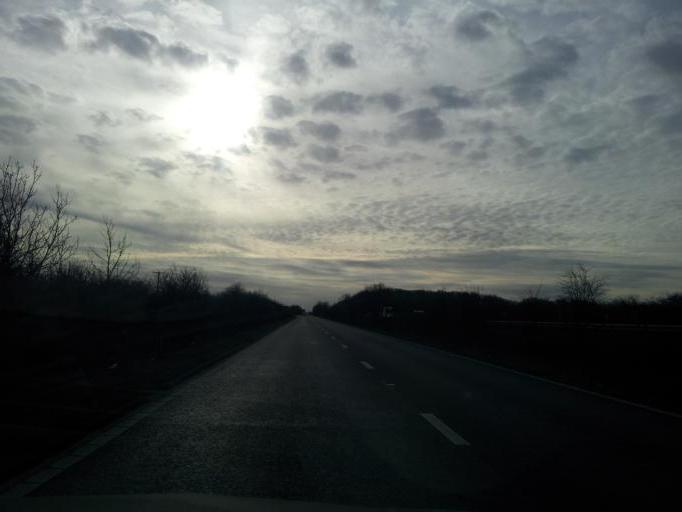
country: GB
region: England
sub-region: District of Rutland
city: Empingham
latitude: 52.6968
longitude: -0.5708
